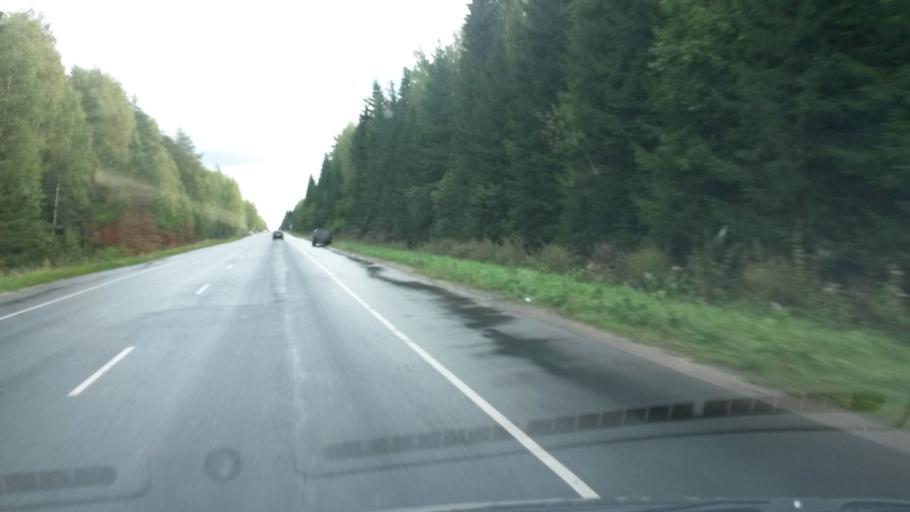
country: RU
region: Ivanovo
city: Kaminskiy
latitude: 57.0399
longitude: 41.3352
